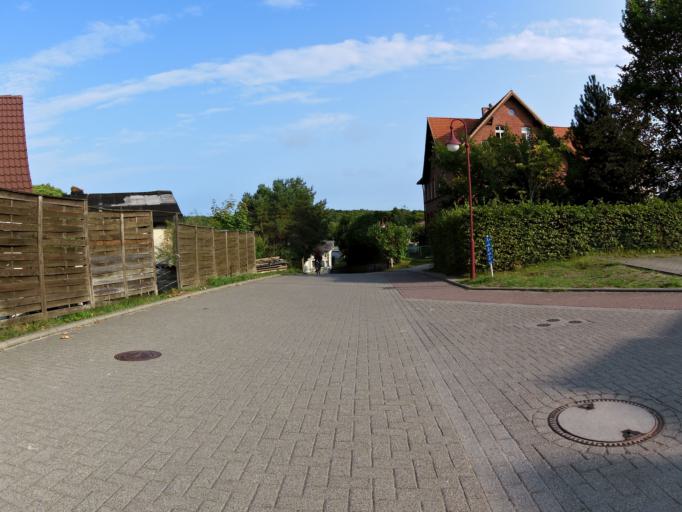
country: DE
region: Mecklenburg-Vorpommern
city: Seebad Bansin
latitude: 53.9562
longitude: 14.1510
